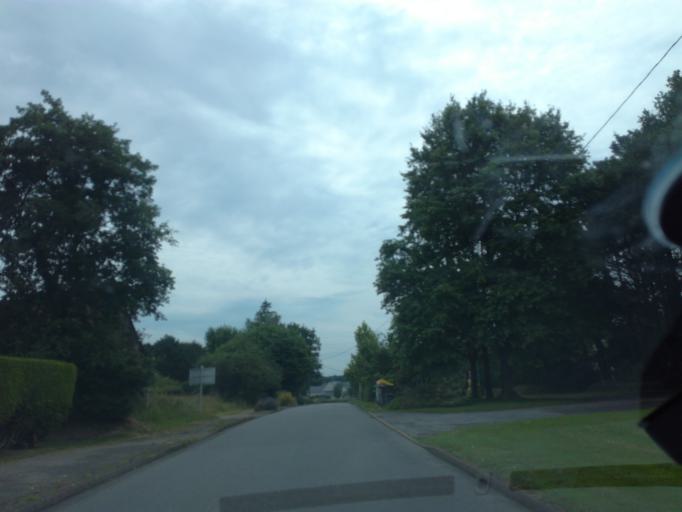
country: FR
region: Brittany
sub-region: Departement du Morbihan
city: Saint-Thuriau
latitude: 48.0215
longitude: -2.9554
